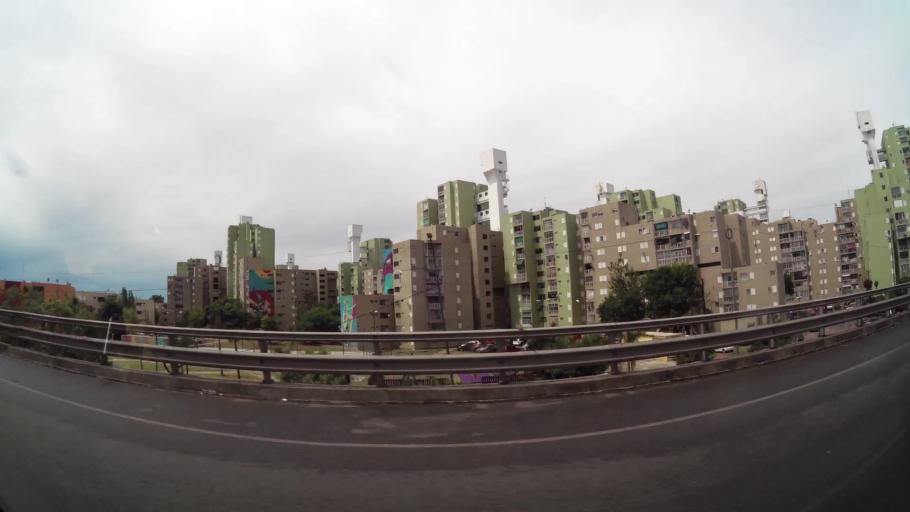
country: AR
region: Buenos Aires F.D.
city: Villa Lugano
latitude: -34.6674
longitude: -58.4473
